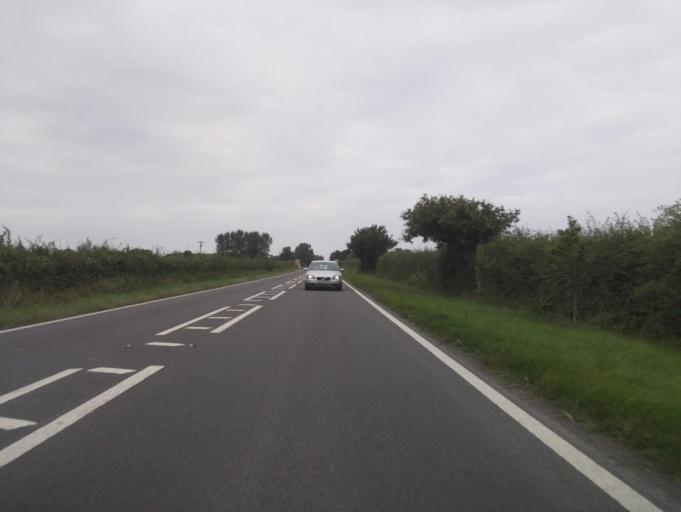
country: GB
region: England
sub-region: Shropshire
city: Shawbury
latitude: 52.7806
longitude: -2.6632
